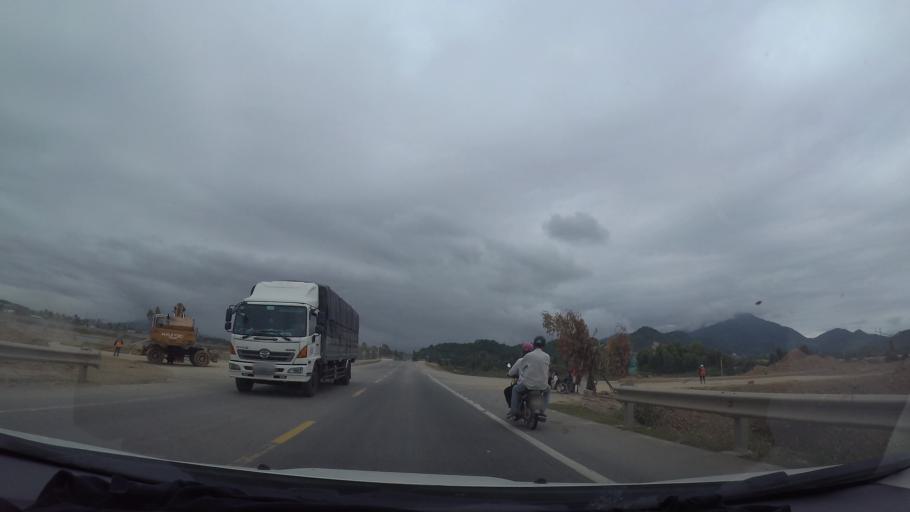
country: VN
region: Da Nang
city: Lien Chieu
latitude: 16.1074
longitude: 108.1034
